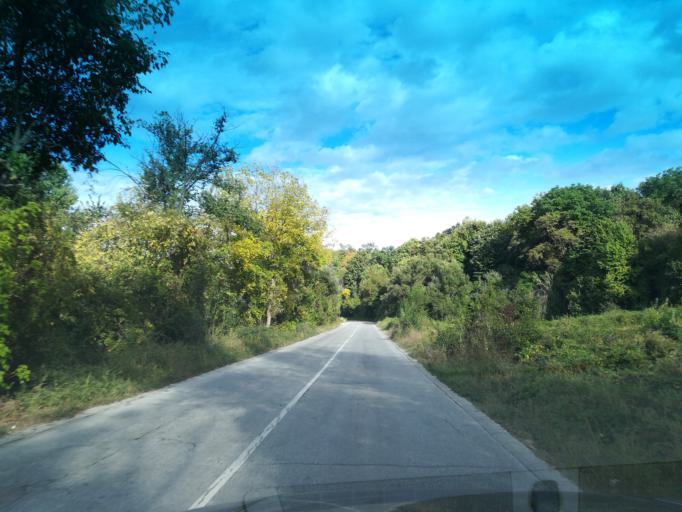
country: BG
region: Pazardzhik
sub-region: Obshtina Peshtera
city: Peshtera
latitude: 42.0457
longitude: 24.3334
